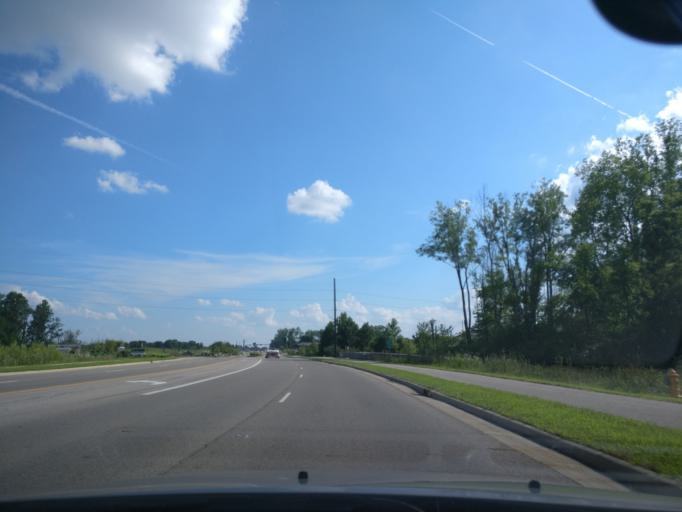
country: US
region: Ohio
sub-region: Warren County
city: Springboro
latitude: 39.6021
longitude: -84.2468
